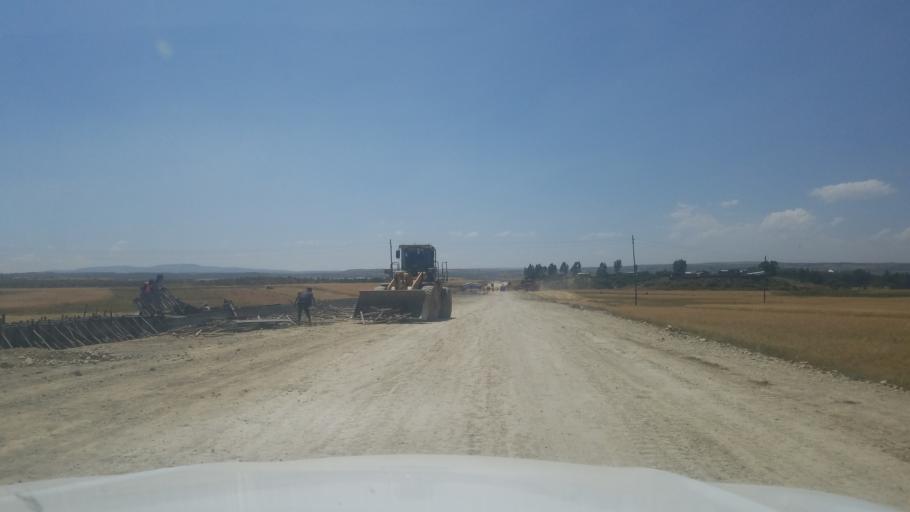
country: ET
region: Tigray
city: Mekele
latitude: 13.7657
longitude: 39.5907
